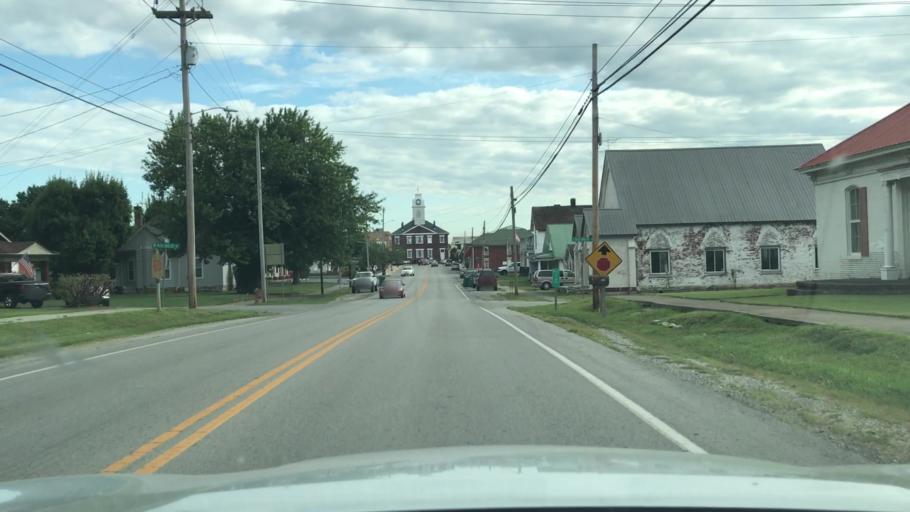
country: US
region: Kentucky
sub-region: Todd County
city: Elkton
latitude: 36.8069
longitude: -87.1548
